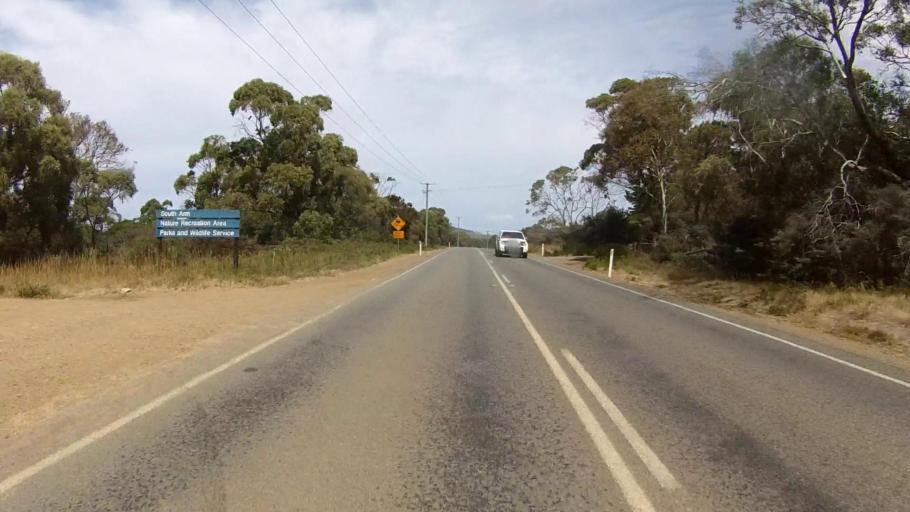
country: AU
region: Tasmania
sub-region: Clarence
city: Sandford
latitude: -43.0208
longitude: 147.4881
